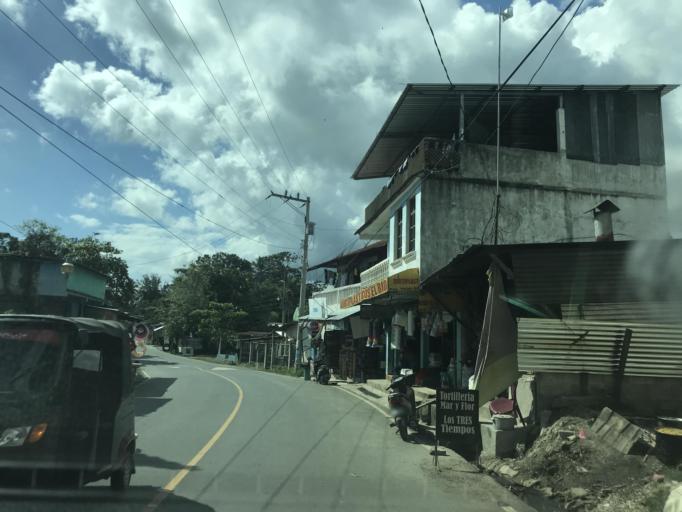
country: GT
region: Izabal
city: Morales
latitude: 15.6582
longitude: -89.0061
